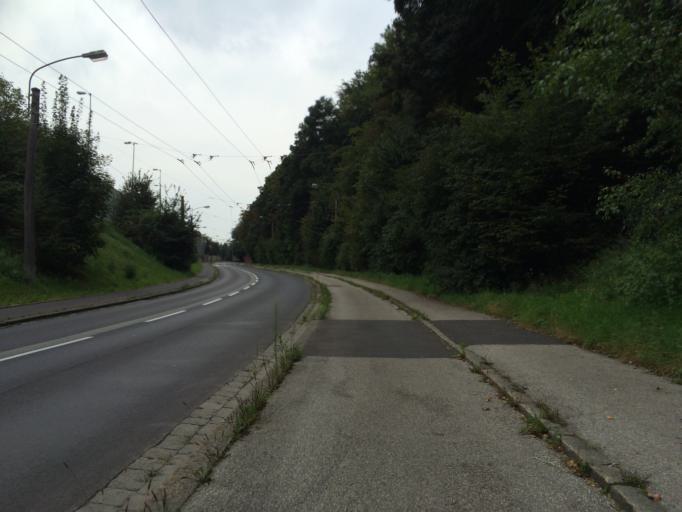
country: AT
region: Upper Austria
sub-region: Linz Stadt
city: Linz
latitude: 48.2780
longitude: 14.2940
